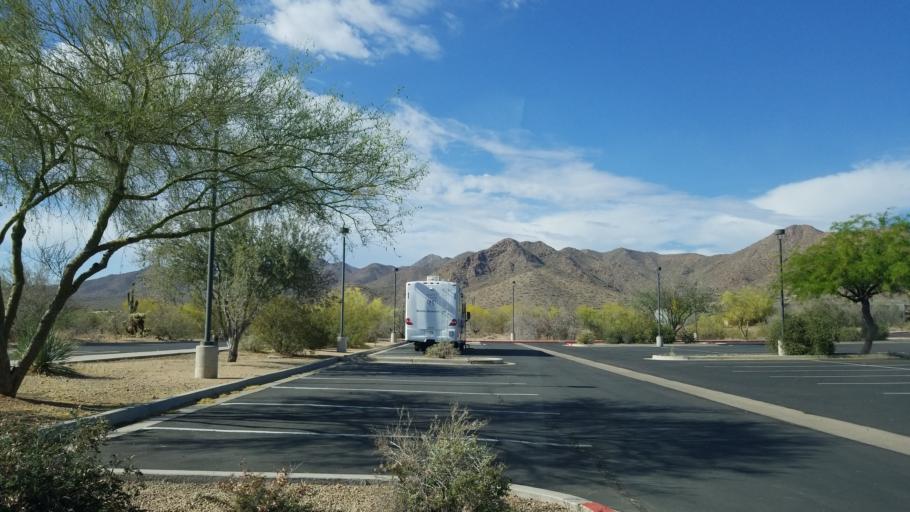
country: US
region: Arizona
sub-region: Maricopa County
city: Fountain Hills
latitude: 33.5846
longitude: -111.7962
